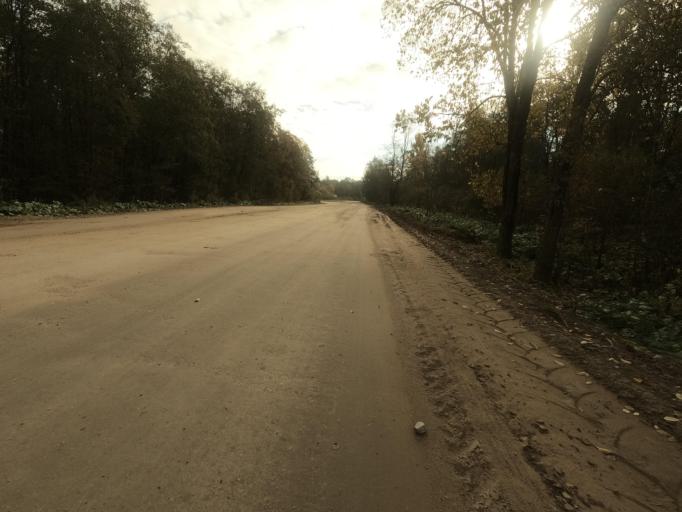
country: RU
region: Novgorod
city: Batetskiy
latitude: 58.7990
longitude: 30.6341
